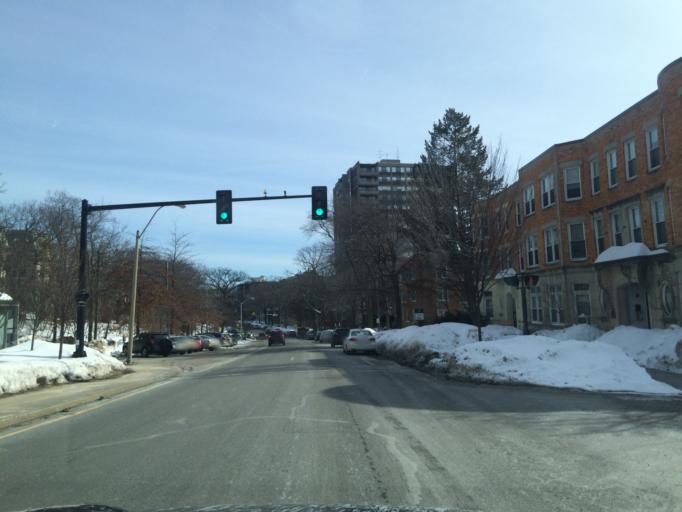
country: US
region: Massachusetts
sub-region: Norfolk County
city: Brookline
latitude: 42.3394
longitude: -71.1317
